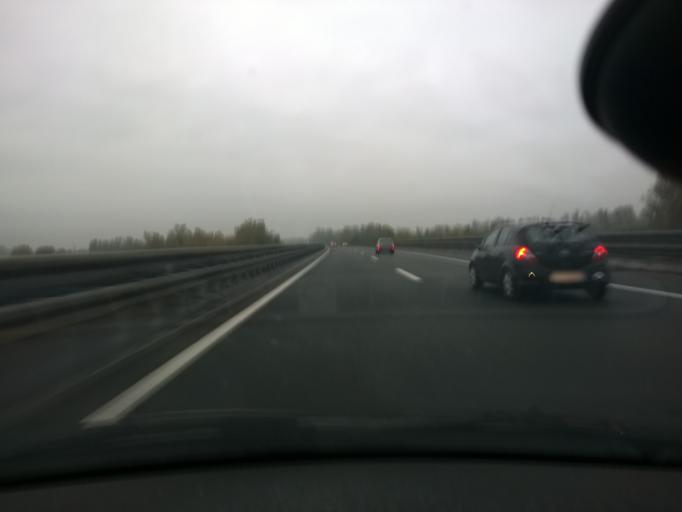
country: HR
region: Zagrebacka
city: Bestovje
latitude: 45.8292
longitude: 15.8192
